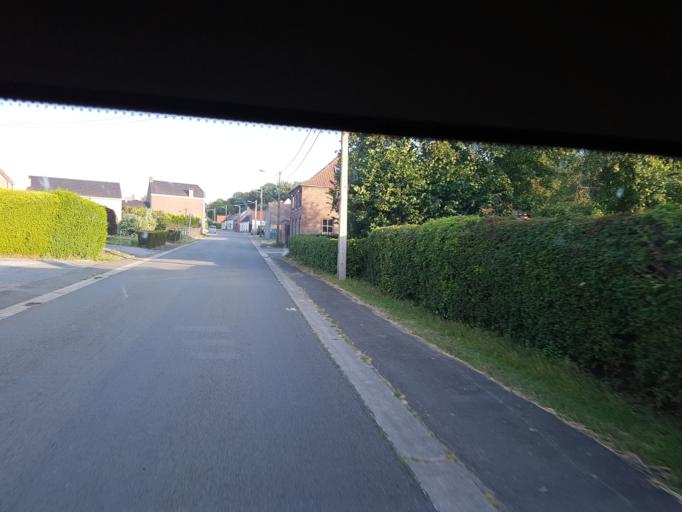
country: FR
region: Nord-Pas-de-Calais
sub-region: Departement du Nord
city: Flines-les-Mortagne
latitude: 50.5430
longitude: 3.5032
